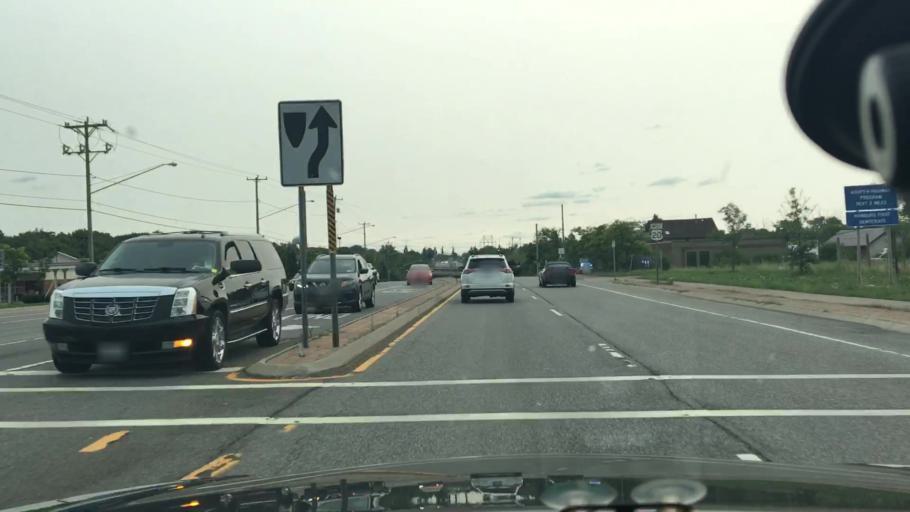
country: US
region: New York
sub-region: Erie County
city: Blasdell
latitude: 42.7699
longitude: -78.8118
